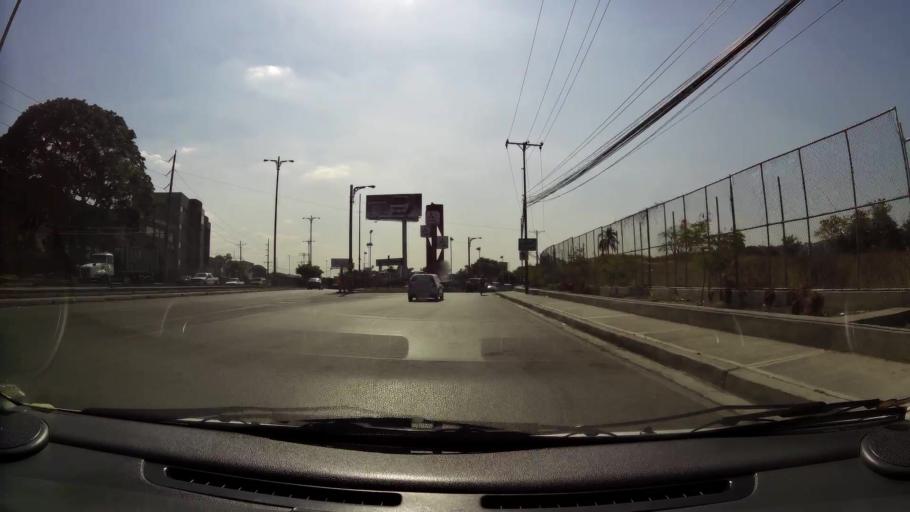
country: EC
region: Guayas
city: Guayaquil
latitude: -2.1643
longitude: -79.9236
